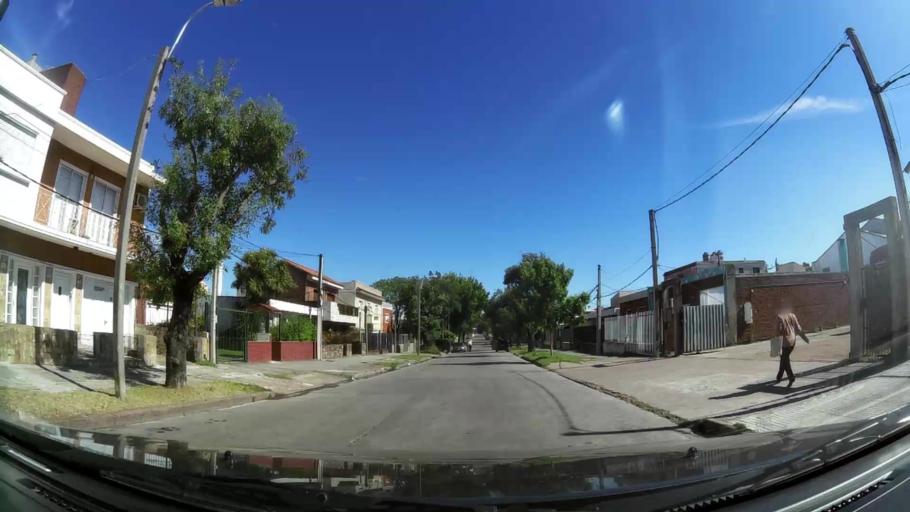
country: UY
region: Montevideo
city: Montevideo
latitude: -34.8934
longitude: -56.1412
